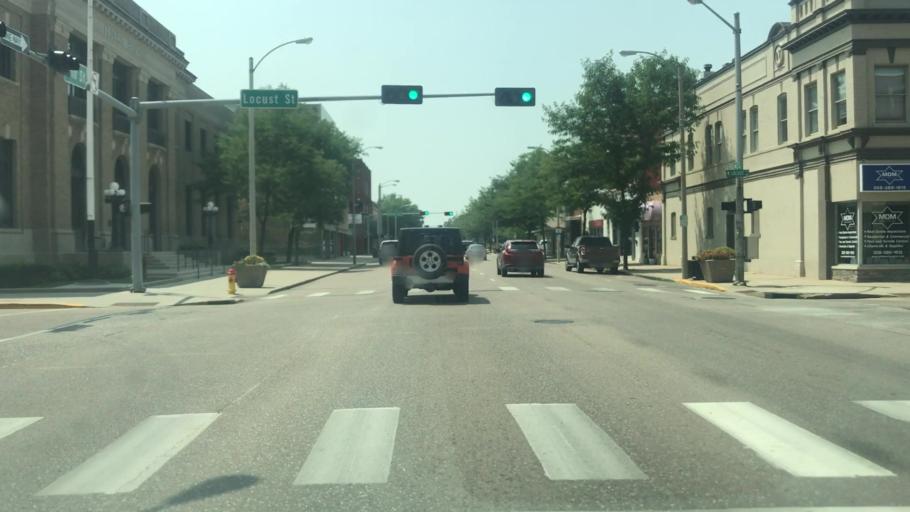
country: US
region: Nebraska
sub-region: Hall County
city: Grand Island
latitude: 40.9246
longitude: -98.3403
